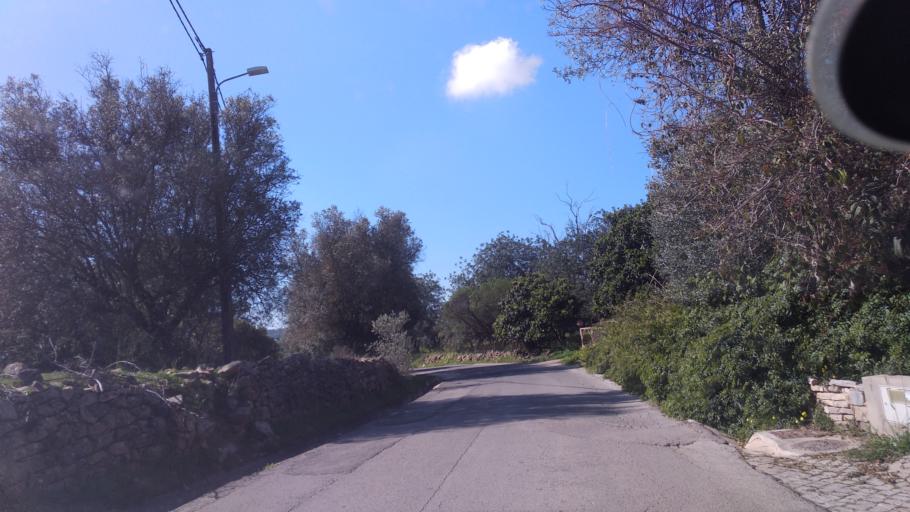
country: PT
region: Faro
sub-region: Sao Bras de Alportel
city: Sao Bras de Alportel
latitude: 37.1276
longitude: -7.9198
